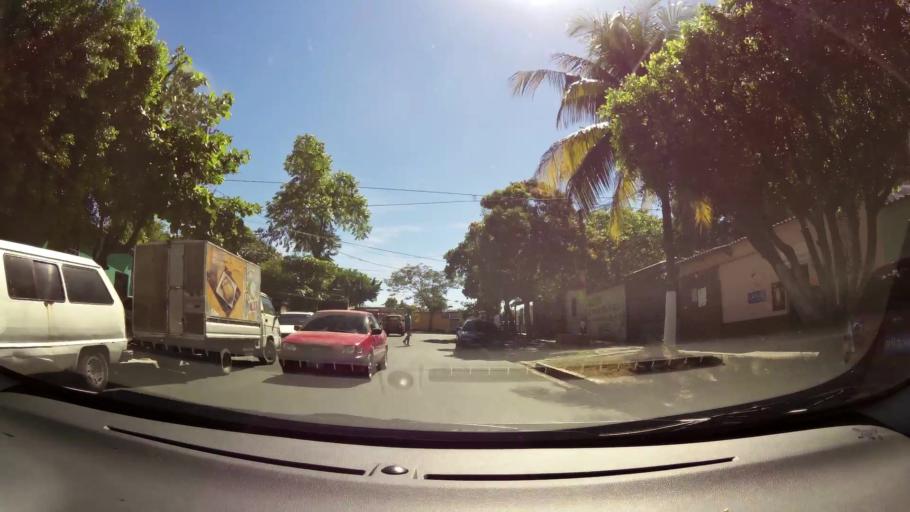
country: SV
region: San Salvador
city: Apopa
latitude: 13.8063
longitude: -89.1795
